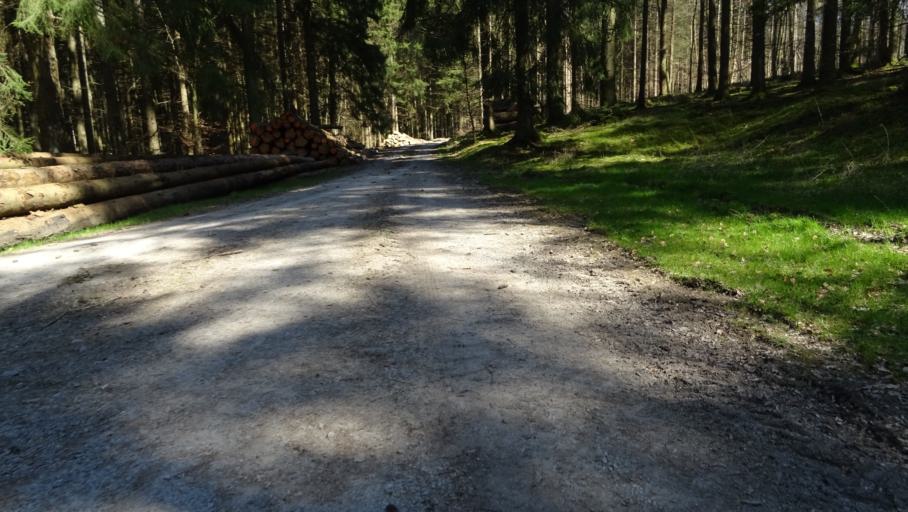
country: DE
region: Baden-Wuerttemberg
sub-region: Regierungsbezirk Stuttgart
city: Roigheim
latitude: 49.4016
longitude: 9.3274
